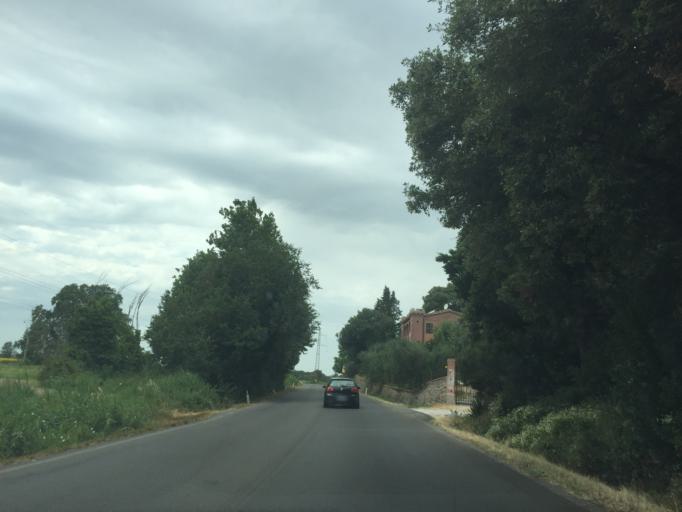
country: IT
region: Tuscany
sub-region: Province of Pisa
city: Gabella
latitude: 43.7264
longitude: 10.4898
